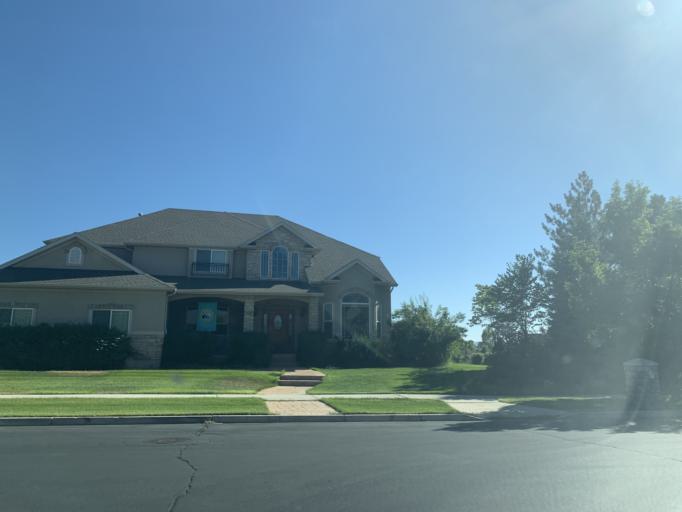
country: US
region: Utah
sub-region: Utah County
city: Provo
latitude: 40.2578
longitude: -111.6874
